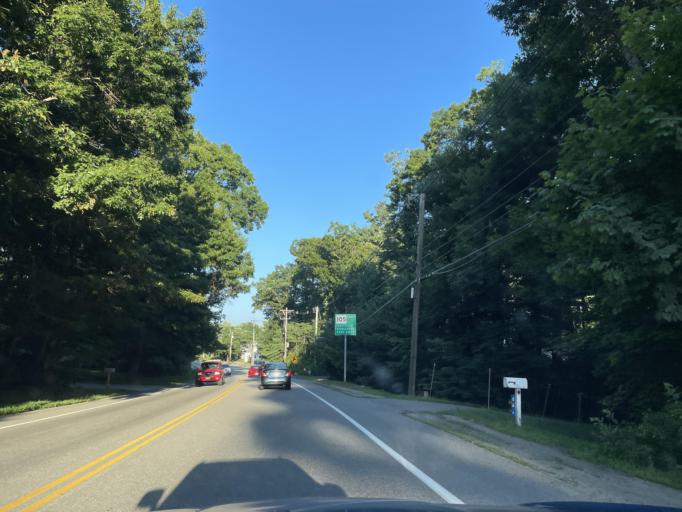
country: US
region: Massachusetts
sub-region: Plymouth County
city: Halifax
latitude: 41.9937
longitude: -70.8757
